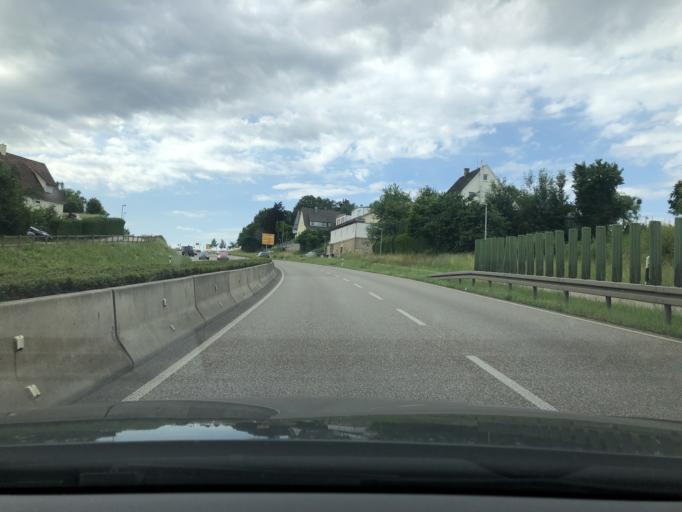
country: DE
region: Baden-Wuerttemberg
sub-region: Regierungsbezirk Stuttgart
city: Nurtingen
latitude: 48.6207
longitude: 9.3267
